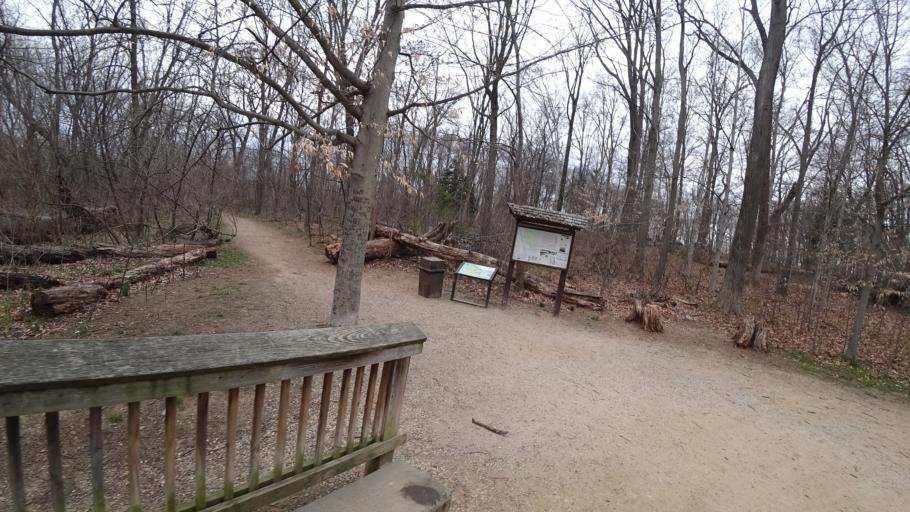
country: US
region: Washington, D.C.
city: Washington, D.C.
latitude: 38.8965
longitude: -77.0651
